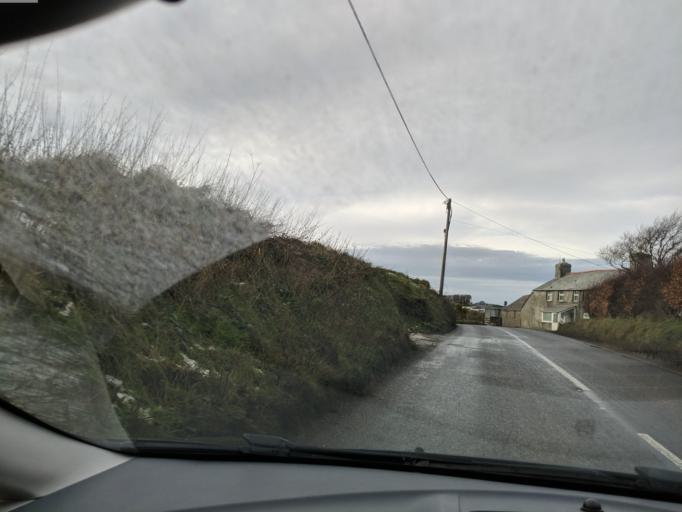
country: GB
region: England
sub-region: Cornwall
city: Jacobstow
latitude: 50.6636
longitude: -4.5824
